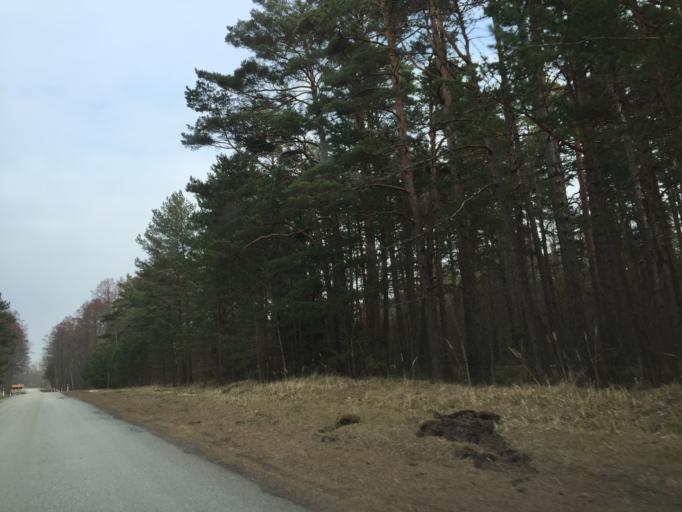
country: LV
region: Salacgrivas
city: Ainazi
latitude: 57.9502
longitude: 24.3923
